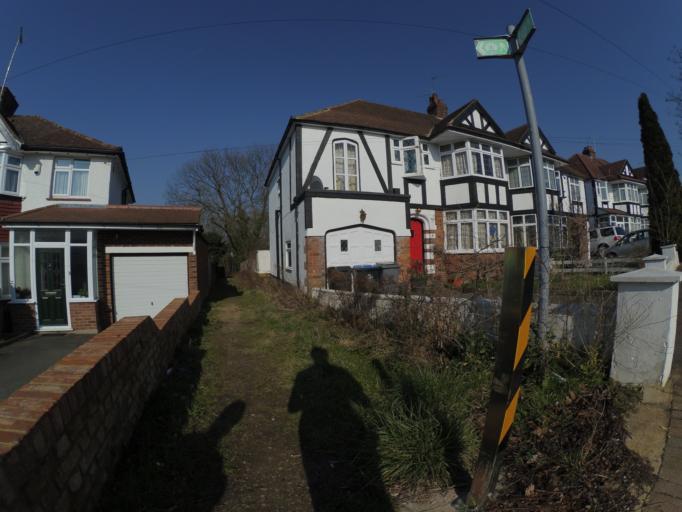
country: GB
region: England
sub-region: Greater London
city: Wembley
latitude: 51.5745
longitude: -0.2877
